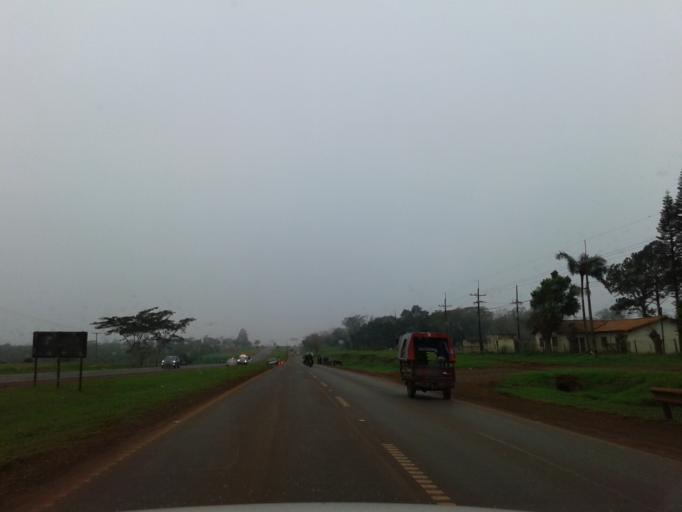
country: PY
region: Alto Parana
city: Colonia Yguazu
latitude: -25.4862
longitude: -54.8705
